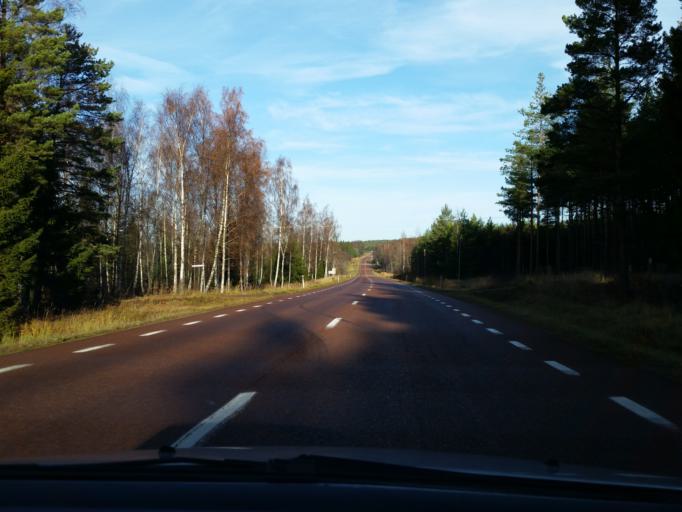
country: AX
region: Alands landsbygd
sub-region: Finstroem
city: Finstroem
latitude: 60.2935
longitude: 19.9534
